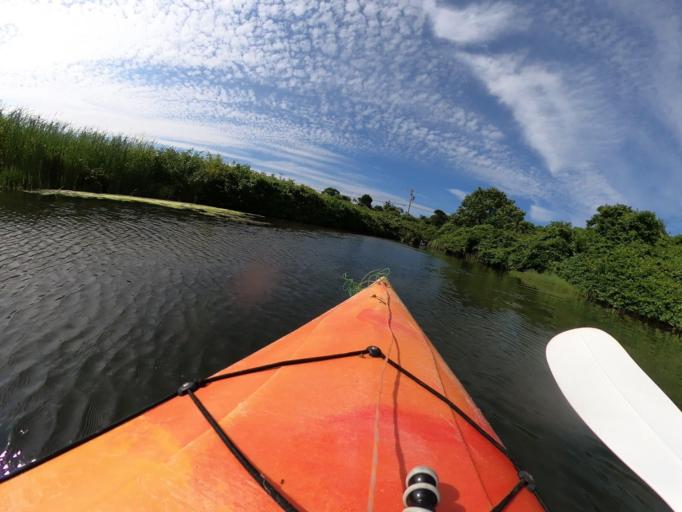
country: US
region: Massachusetts
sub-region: Dukes County
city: West Tisbury
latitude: 41.3278
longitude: -70.7865
